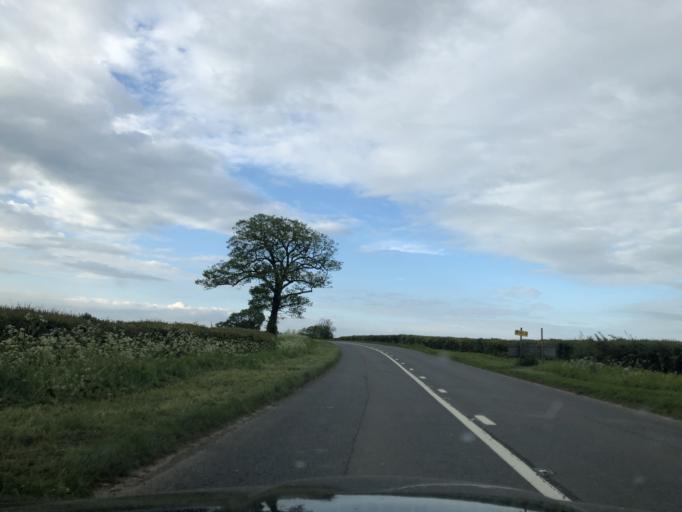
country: GB
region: England
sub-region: Gloucestershire
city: Moreton in Marsh
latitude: 51.9702
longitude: -1.7089
